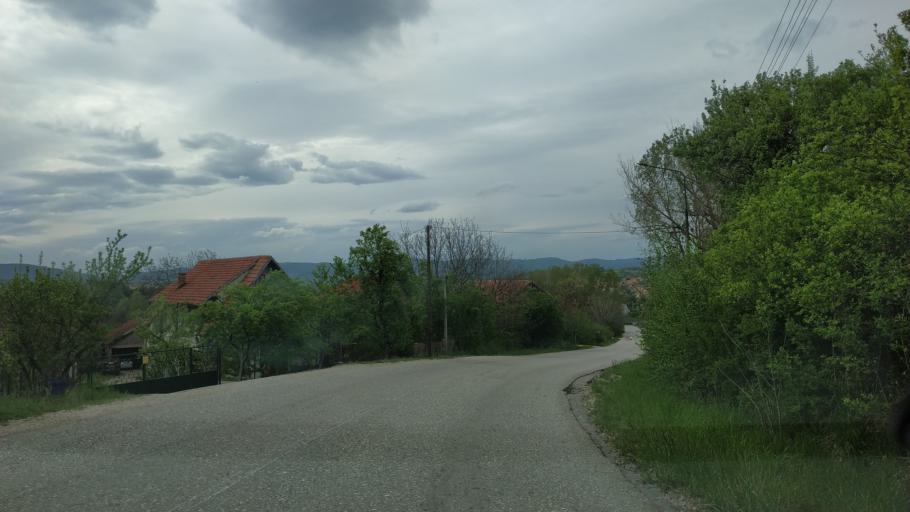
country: RS
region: Central Serbia
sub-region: Zajecarski Okrug
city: Soko Banja
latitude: 43.6430
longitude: 21.8889
